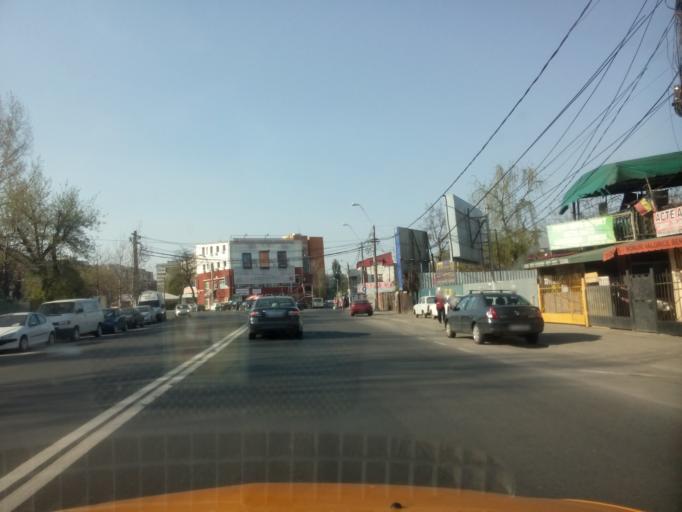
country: RO
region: Ilfov
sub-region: Comuna Popesti-Leordeni
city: Popesti-Leordeni
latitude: 44.4062
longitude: 26.1421
